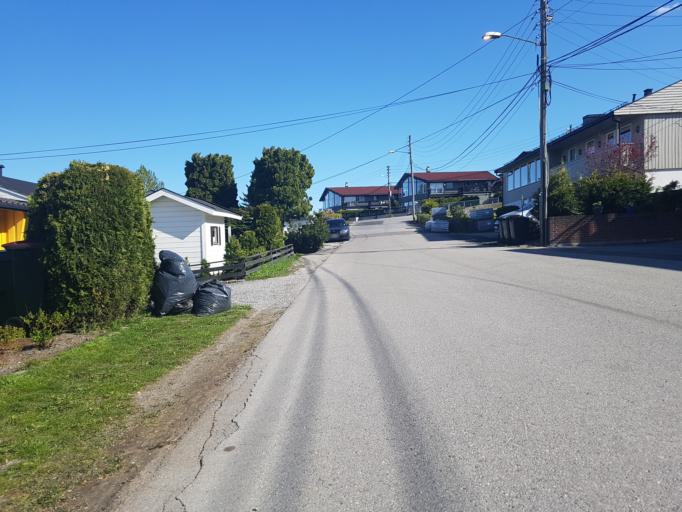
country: NO
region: Buskerud
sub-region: Drammen
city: Drammen
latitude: 59.7221
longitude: 10.2118
